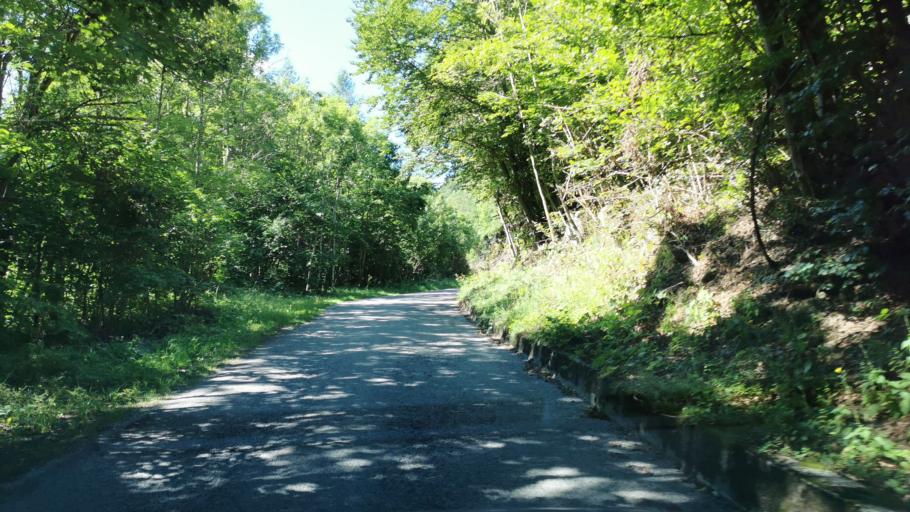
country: IT
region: Piedmont
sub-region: Provincia di Cuneo
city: Entracque
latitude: 44.2143
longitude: 7.3831
